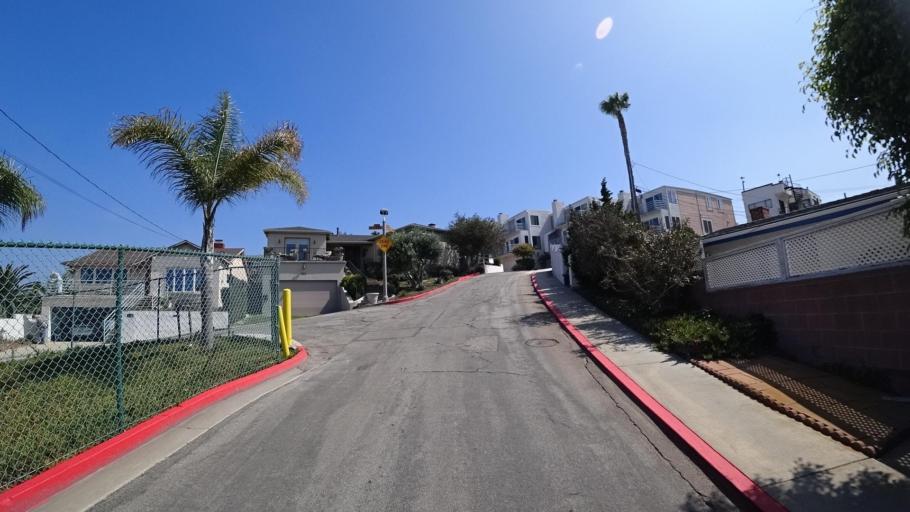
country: US
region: California
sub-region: Los Angeles County
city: Hermosa Beach
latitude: 33.8641
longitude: -118.3911
